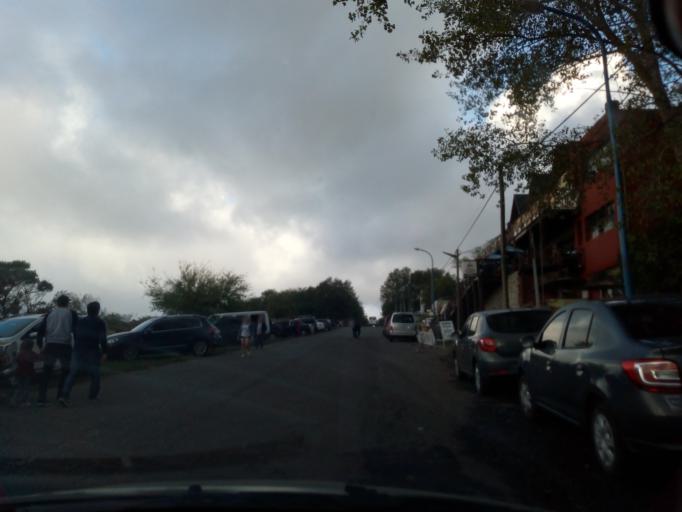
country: AR
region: Buenos Aires
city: Mar del Plata
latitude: -37.9456
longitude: -57.7811
